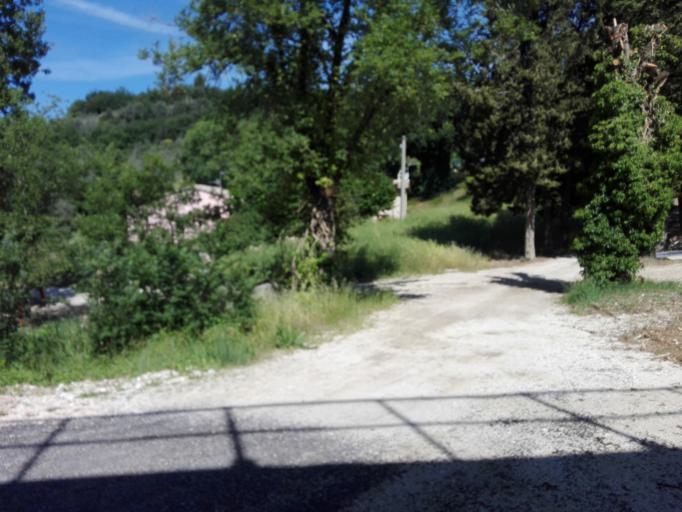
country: IT
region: Umbria
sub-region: Provincia di Perugia
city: Foligno
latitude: 42.9570
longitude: 12.7348
